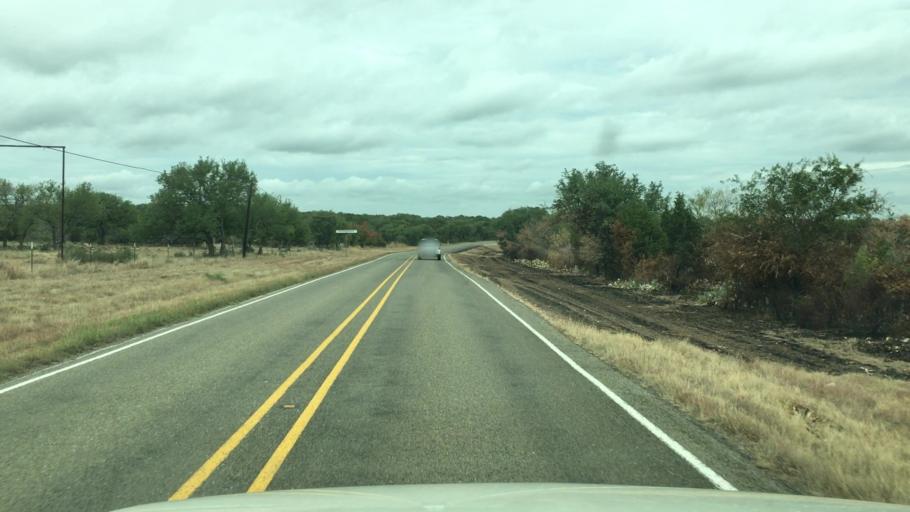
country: US
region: Texas
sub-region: Llano County
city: Horseshoe Bay
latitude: 30.4830
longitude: -98.4272
